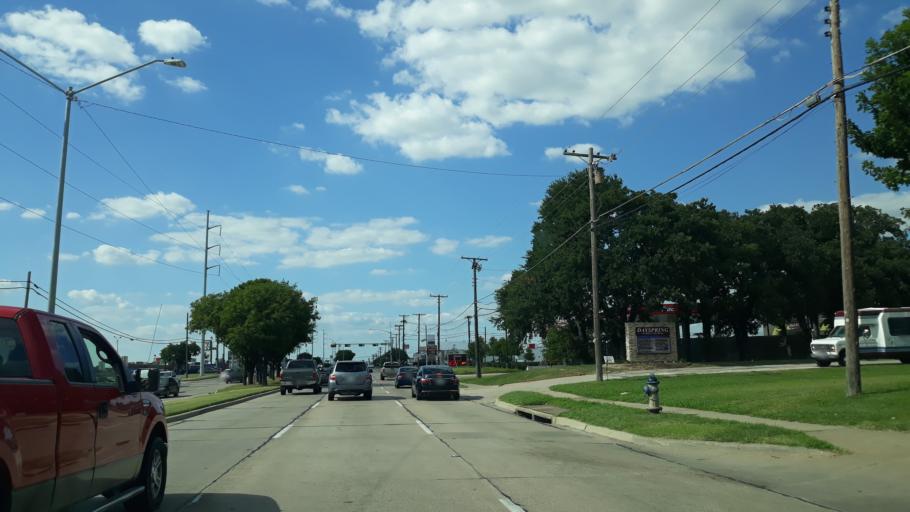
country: US
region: Texas
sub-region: Dallas County
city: Irving
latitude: 32.8203
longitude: -96.9937
